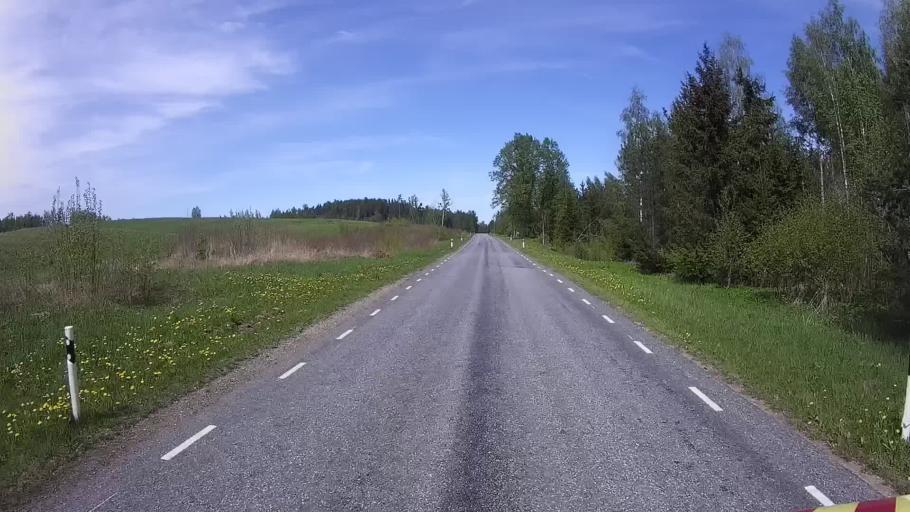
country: EE
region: Valgamaa
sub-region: Valga linn
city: Valga
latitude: 57.6701
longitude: 26.2846
